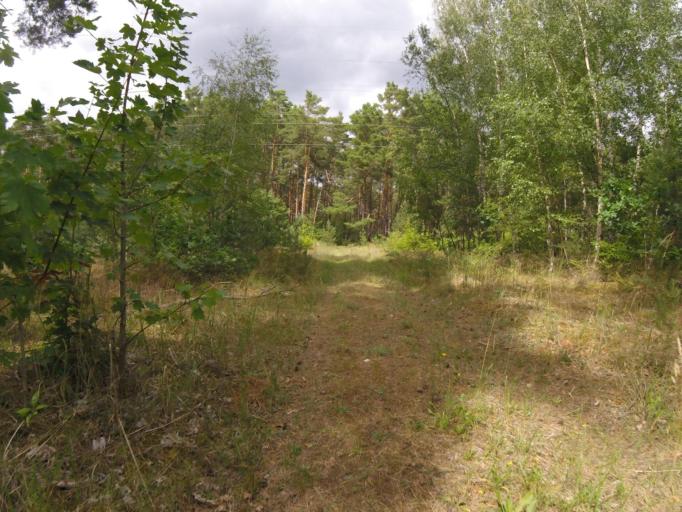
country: DE
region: Brandenburg
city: Wildau
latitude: 52.3330
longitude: 13.6687
